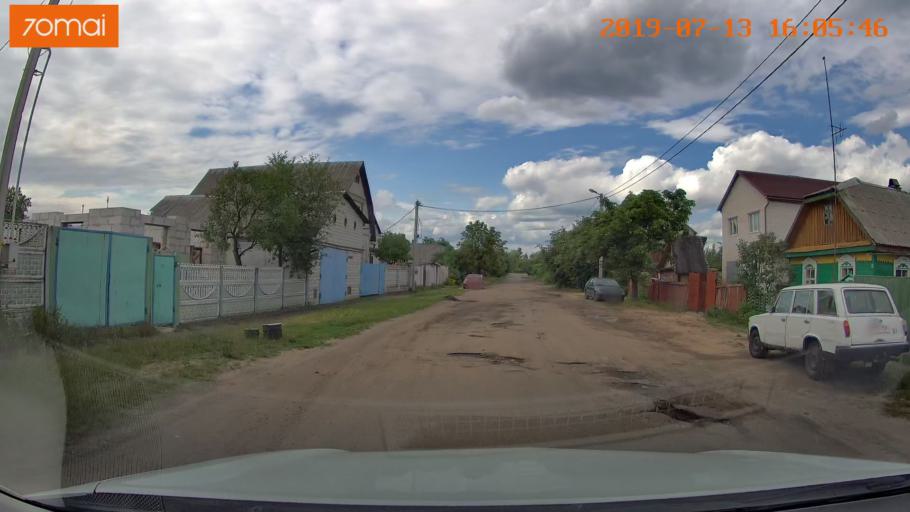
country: BY
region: Mogilev
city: Babruysk
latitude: 53.1505
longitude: 29.2050
